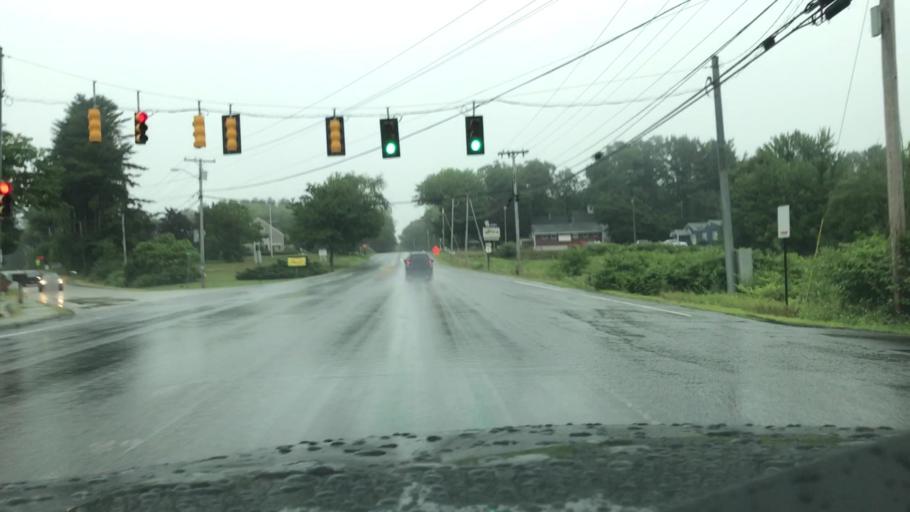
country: US
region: Maine
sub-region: York County
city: Kennebunk
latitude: 43.4075
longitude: -70.5230
